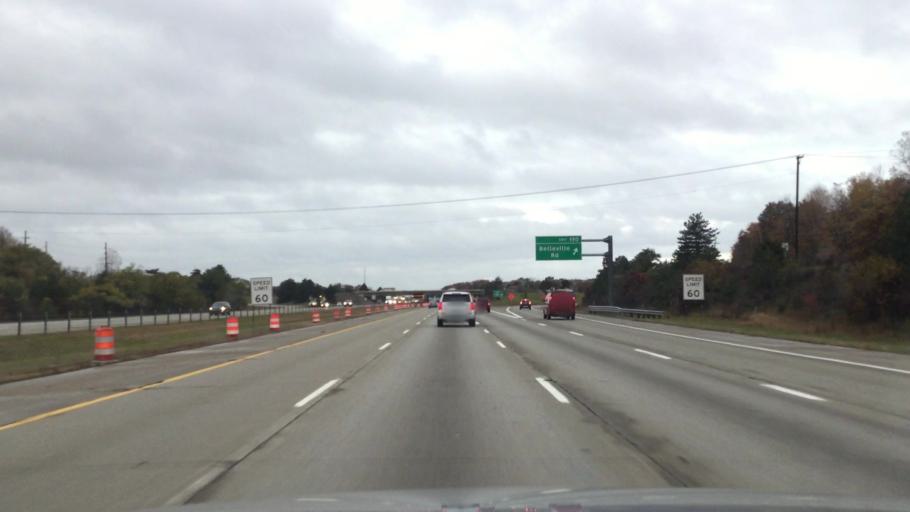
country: US
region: Michigan
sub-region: Wayne County
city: Belleville
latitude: 42.2200
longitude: -83.4775
